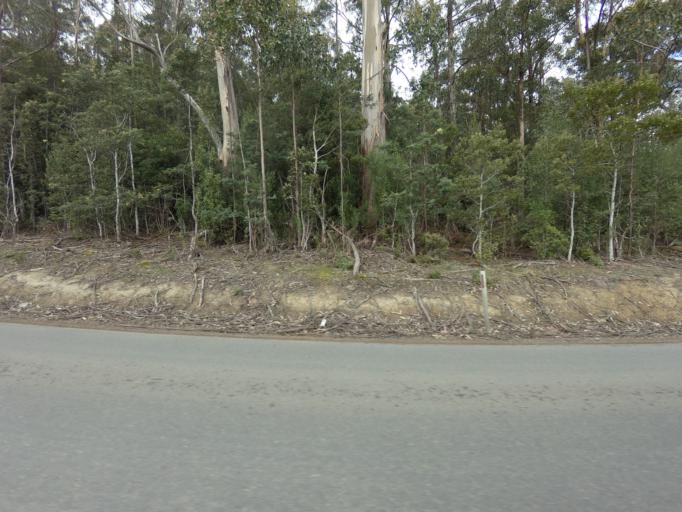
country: AU
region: Tasmania
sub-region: Huon Valley
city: Cygnet
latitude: -43.2667
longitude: 147.0109
